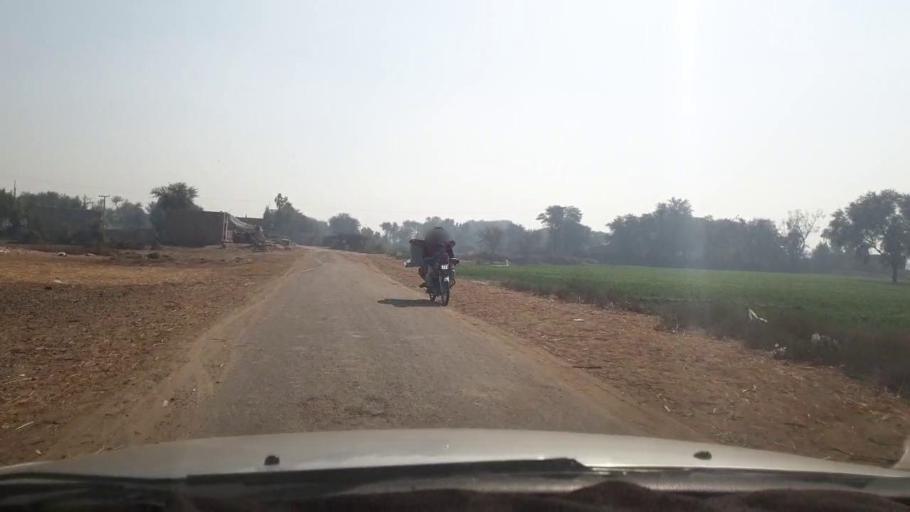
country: PK
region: Sindh
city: Khanpur
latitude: 27.7305
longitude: 69.5145
